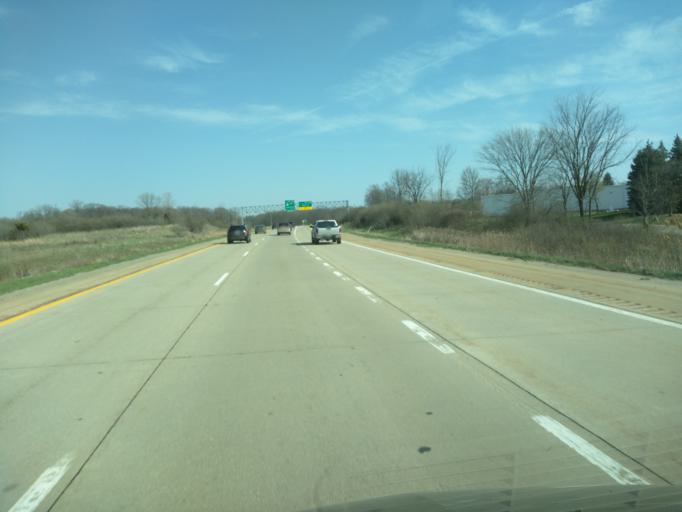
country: US
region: Michigan
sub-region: Kent County
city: Forest Hills
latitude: 42.9054
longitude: -85.5258
